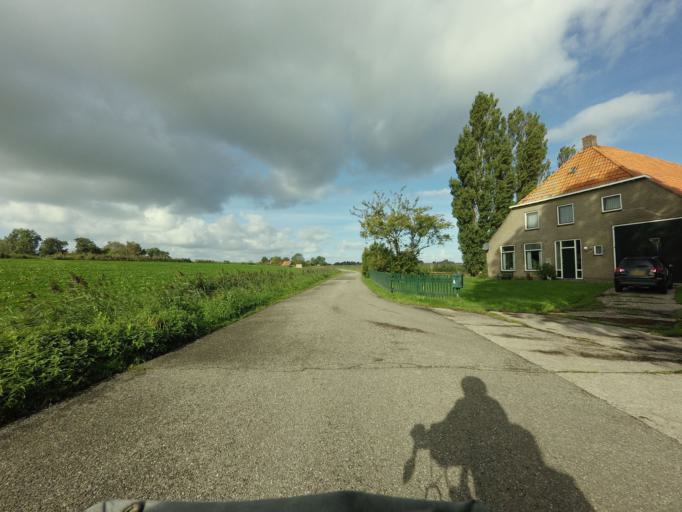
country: NL
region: Friesland
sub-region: Sudwest Fryslan
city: Makkum
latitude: 53.0560
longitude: 5.4310
